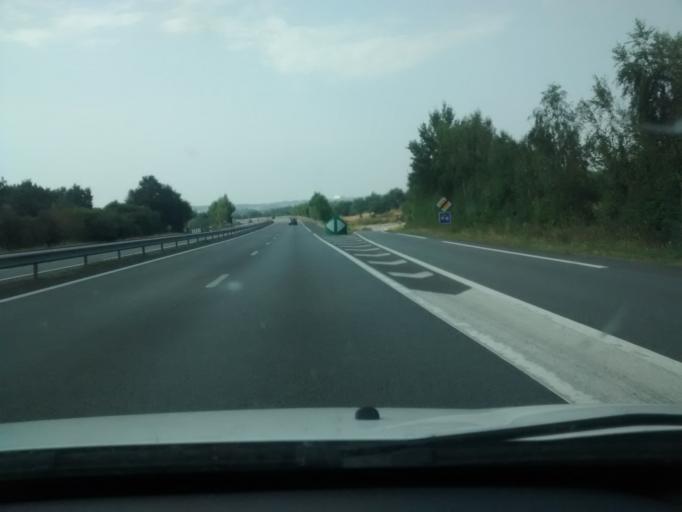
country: FR
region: Brittany
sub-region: Departement d'Ille-et-Vilaine
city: La Dominelais
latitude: 47.7849
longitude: -1.6978
